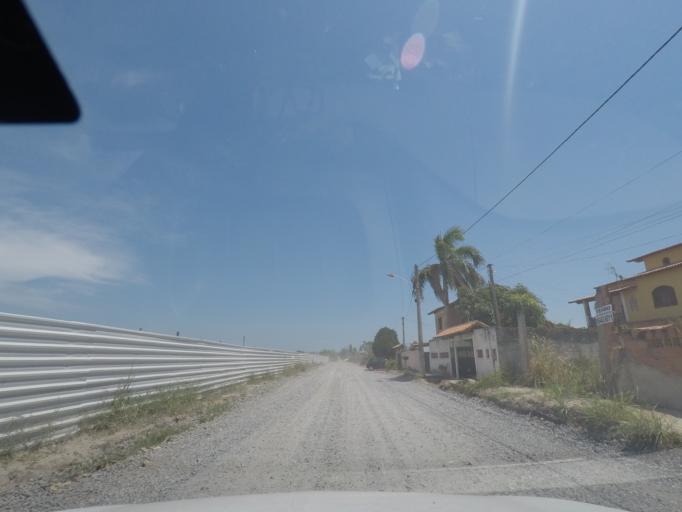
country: BR
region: Rio de Janeiro
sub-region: Marica
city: Marica
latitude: -22.9578
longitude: -42.9541
